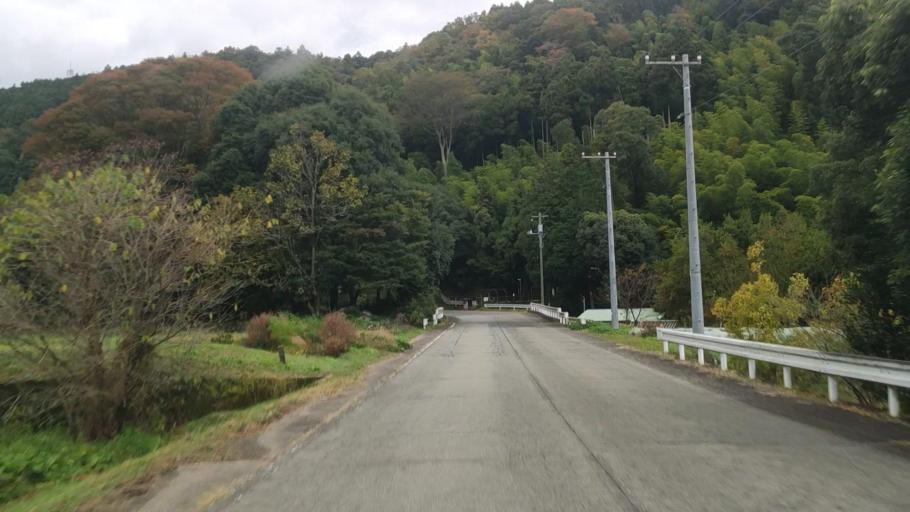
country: JP
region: Shizuoka
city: Ito
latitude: 34.9250
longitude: 138.9979
